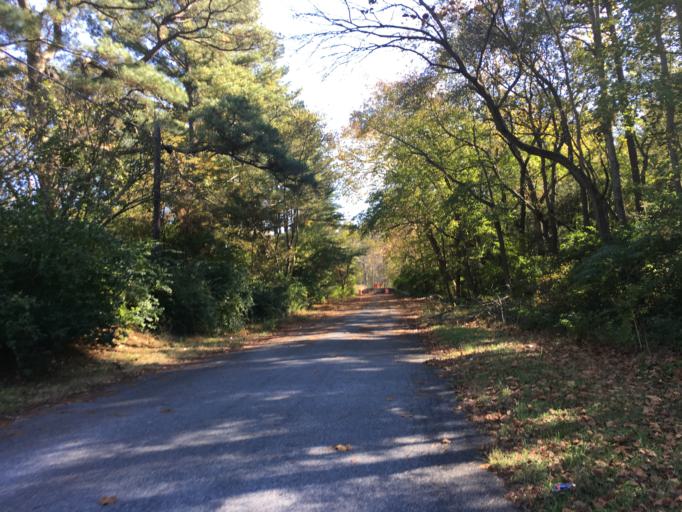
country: US
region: Maryland
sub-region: Wicomico County
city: Hebron
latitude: 38.4631
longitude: -75.7356
